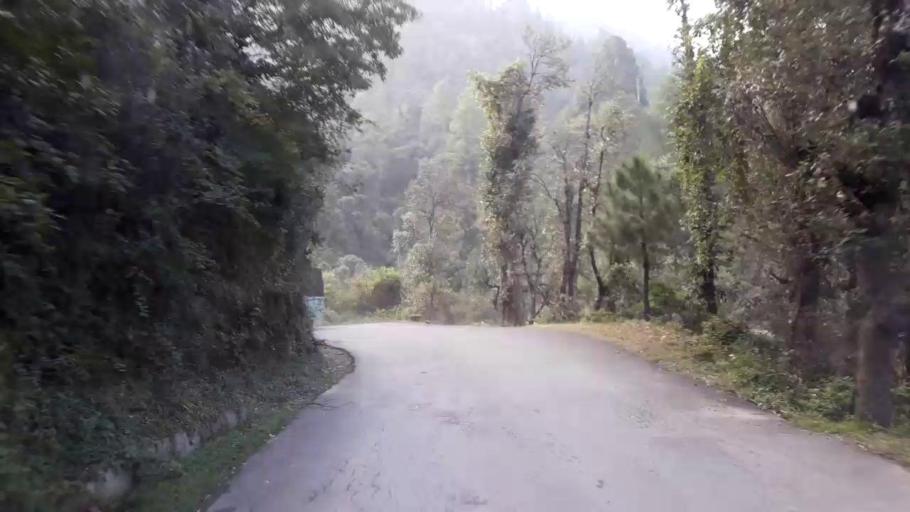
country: IN
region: Himachal Pradesh
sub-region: Shimla
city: Shimla
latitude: 31.0501
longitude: 77.1491
